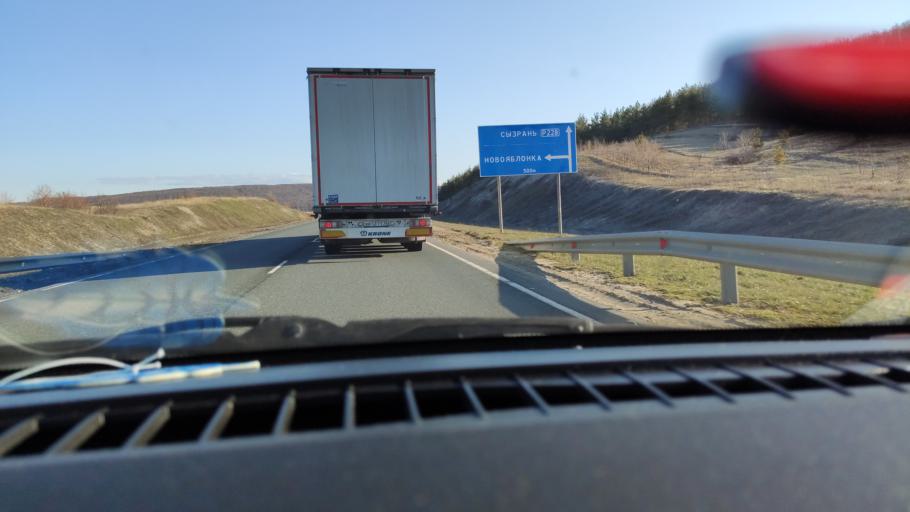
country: RU
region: Saratov
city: Alekseyevka
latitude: 52.3850
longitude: 47.9740
